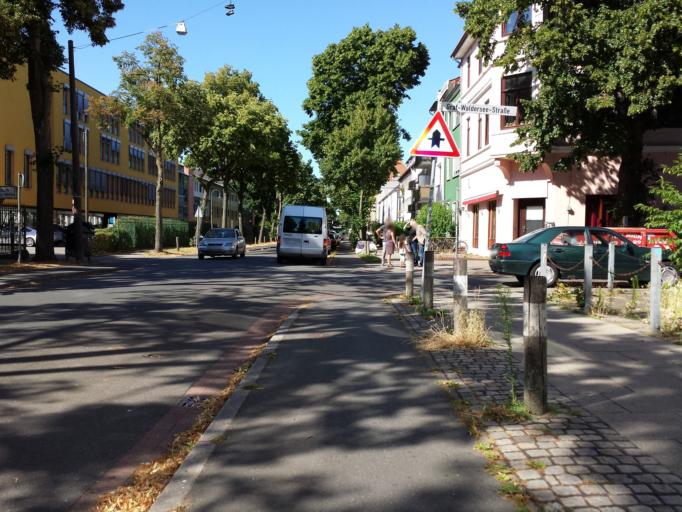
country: DE
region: Bremen
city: Bremen
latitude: 53.0732
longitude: 8.8433
